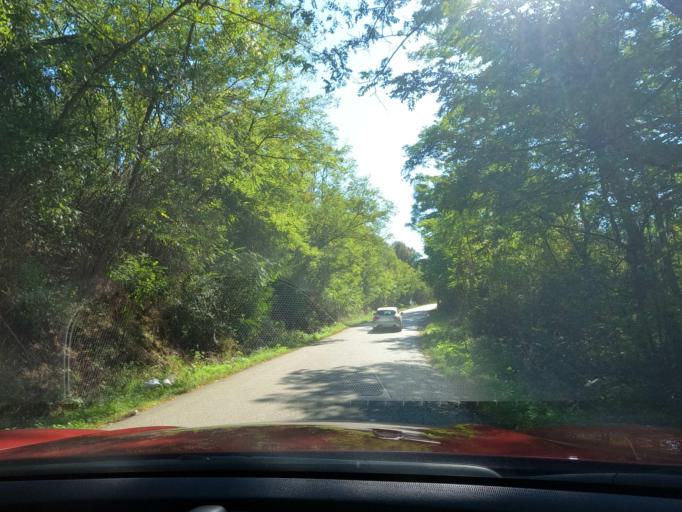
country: RS
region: Central Serbia
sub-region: Raski Okrug
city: Kraljevo
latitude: 43.7705
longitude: 20.6609
